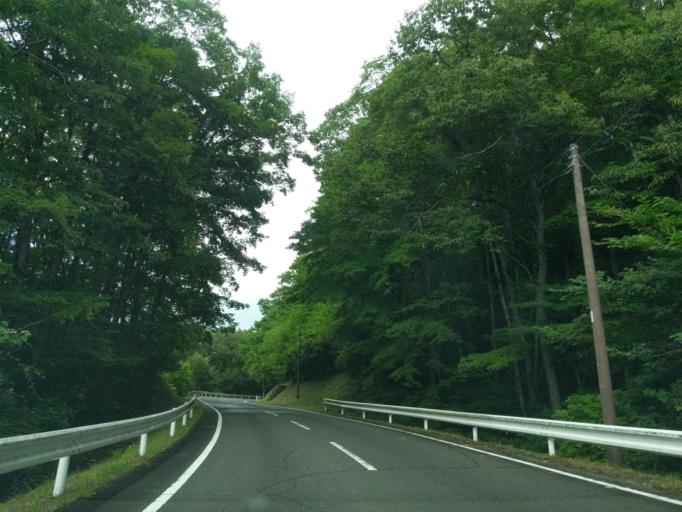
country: JP
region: Tochigi
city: Kuroiso
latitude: 37.2451
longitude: 140.0731
